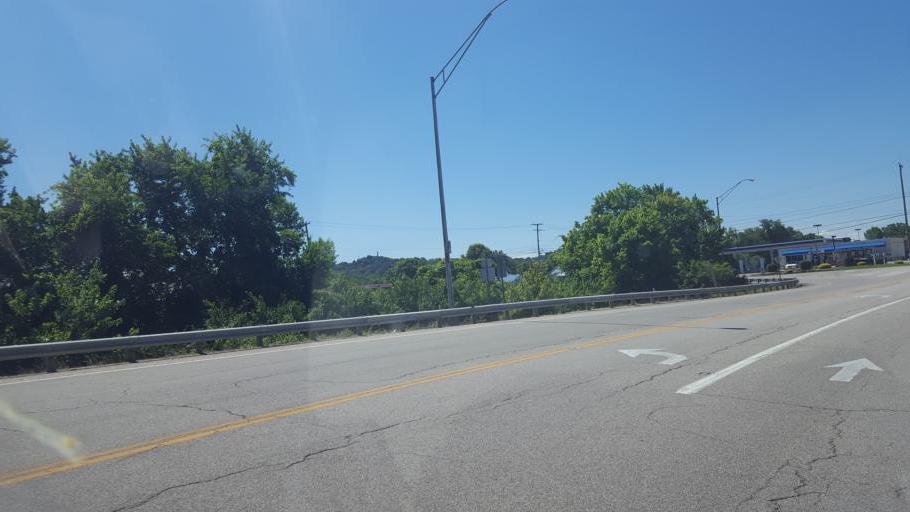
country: US
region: West Virginia
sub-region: Cabell County
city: Huntington
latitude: 38.4399
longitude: -82.3867
